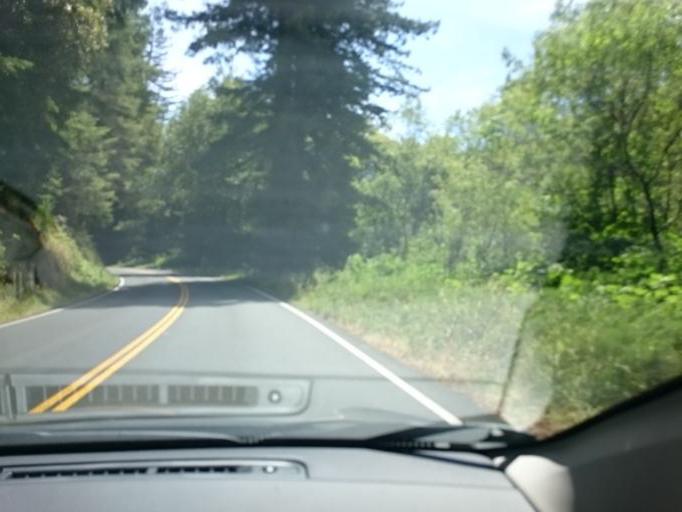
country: US
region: California
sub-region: Mendocino County
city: Fort Bragg
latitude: 39.1642
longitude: -123.6581
